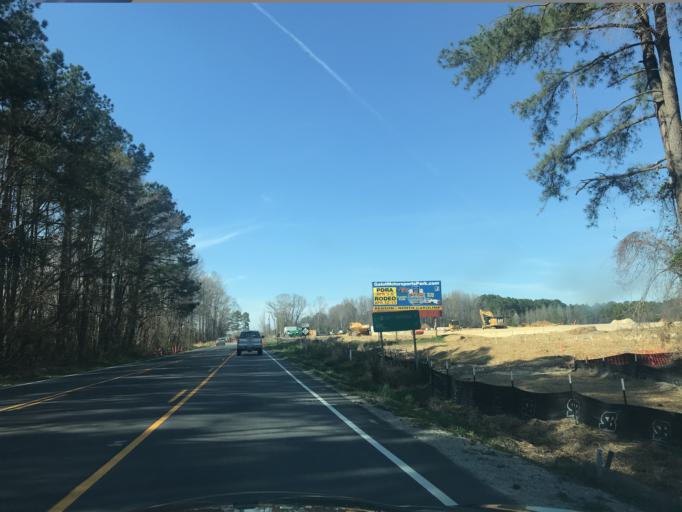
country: US
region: North Carolina
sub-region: Harnett County
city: Angier
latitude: 35.5322
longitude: -78.7451
